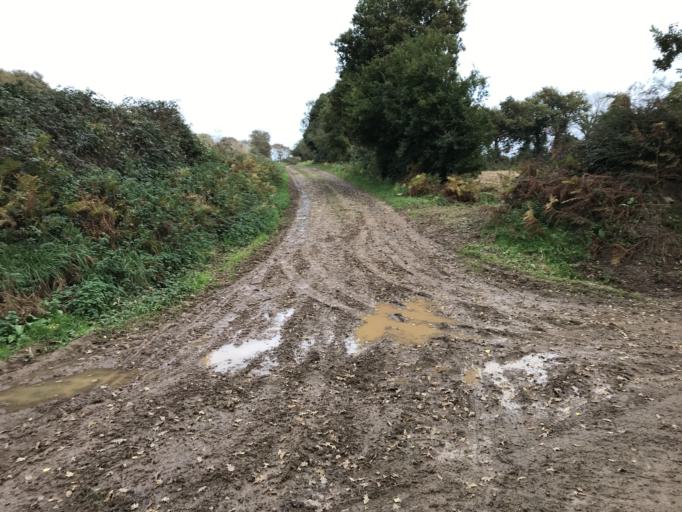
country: FR
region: Brittany
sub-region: Departement du Finistere
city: Irvillac
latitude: 48.3500
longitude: -4.2176
